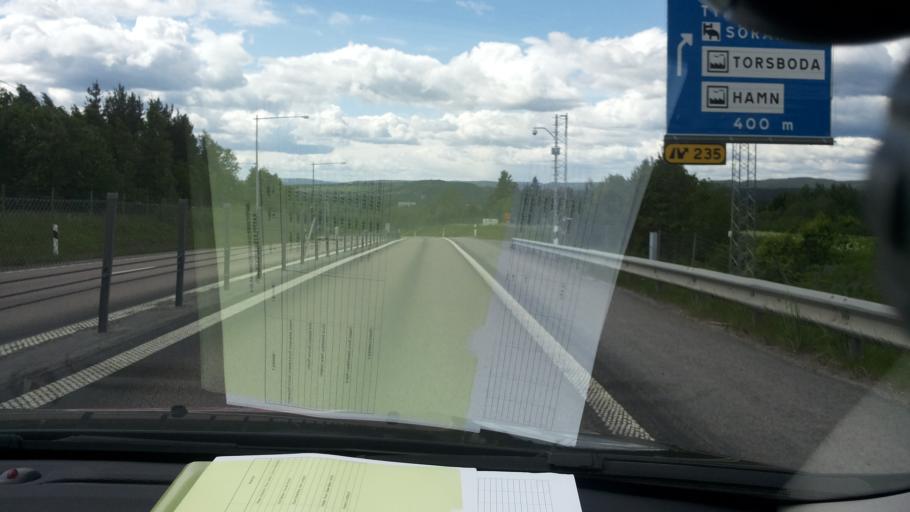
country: SE
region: Vaesternorrland
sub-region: Timra Kommun
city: Soraker
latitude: 62.5293
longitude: 17.4847
